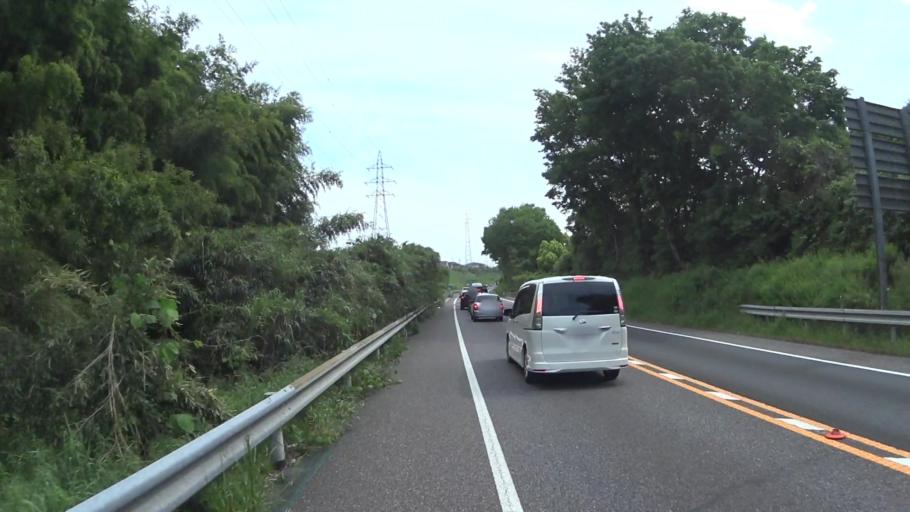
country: JP
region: Shiga Prefecture
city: Kitahama
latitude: 35.1063
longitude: 135.8950
